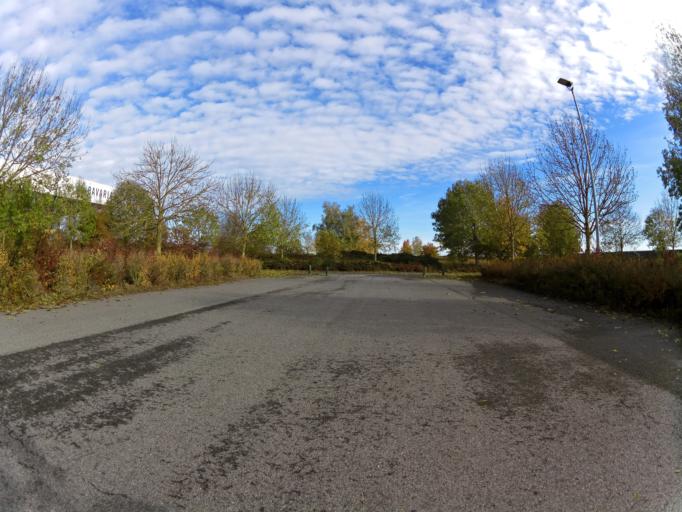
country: DE
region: Bavaria
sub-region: Regierungsbezirk Unterfranken
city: Giebelstadt
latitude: 49.6506
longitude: 9.9581
